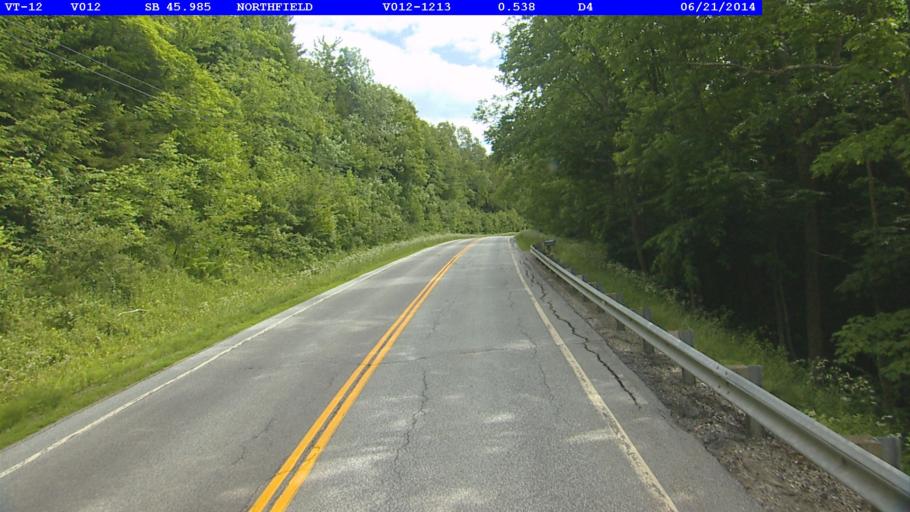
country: US
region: Vermont
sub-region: Washington County
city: Northfield
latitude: 44.1002
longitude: -72.6440
